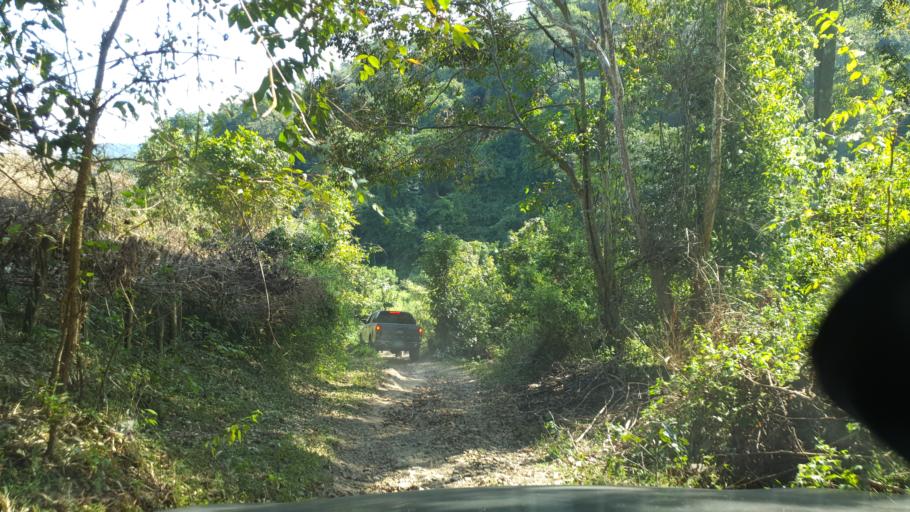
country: TH
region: Mae Hong Son
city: Mae Hi
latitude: 19.2987
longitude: 98.7029
